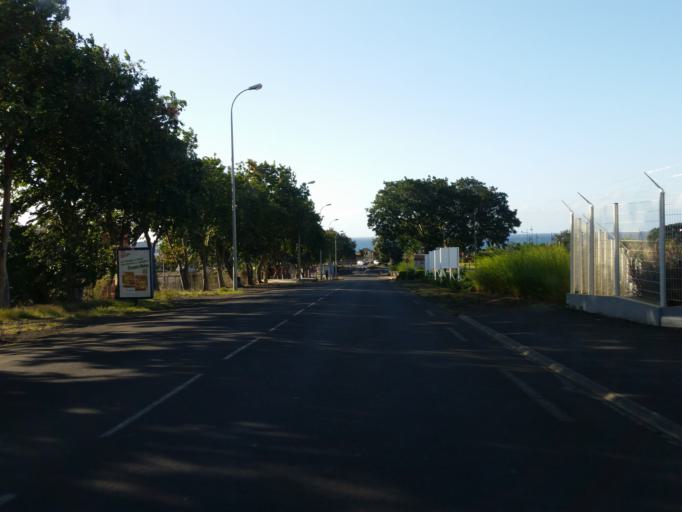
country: RE
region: Reunion
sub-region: Reunion
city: Saint-Denis
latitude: -20.8896
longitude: 55.4719
